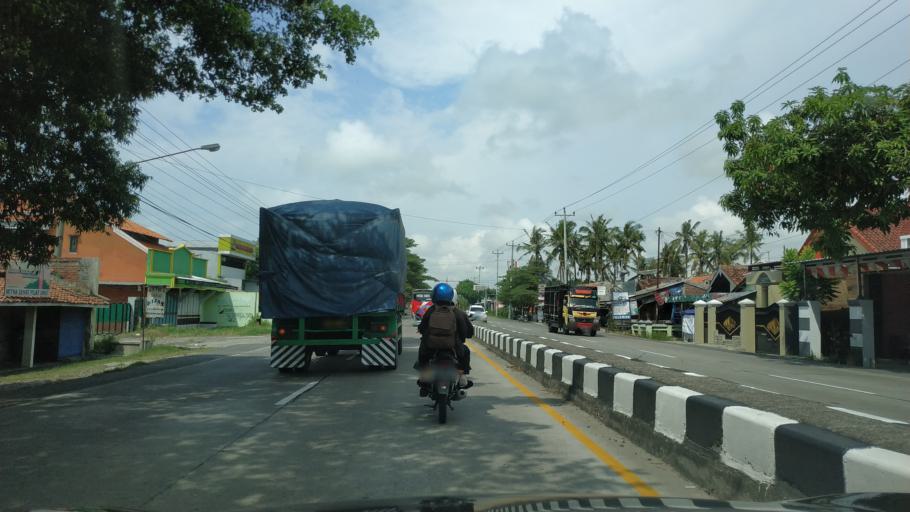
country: ID
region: Central Java
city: Tarub
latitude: -6.8718
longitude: 109.2411
